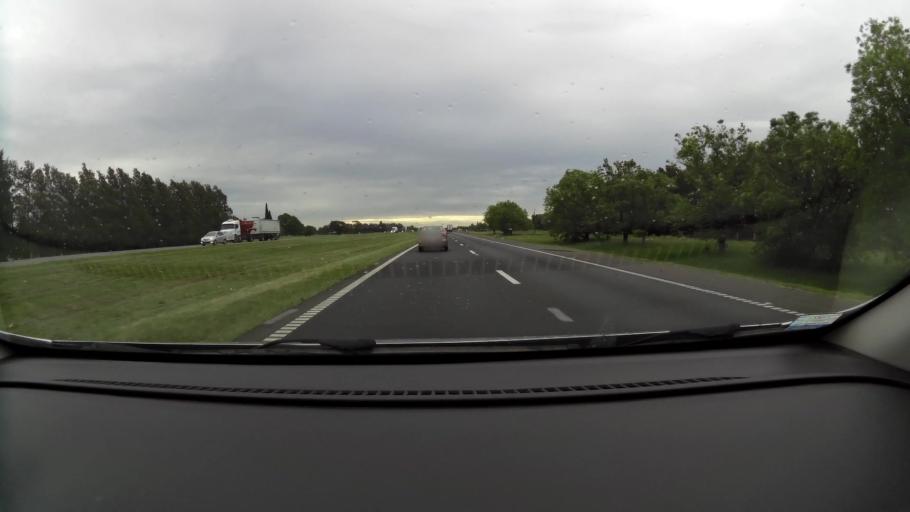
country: AR
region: Buenos Aires
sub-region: Partido de San Pedro
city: San Pedro
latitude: -33.7382
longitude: -59.7916
